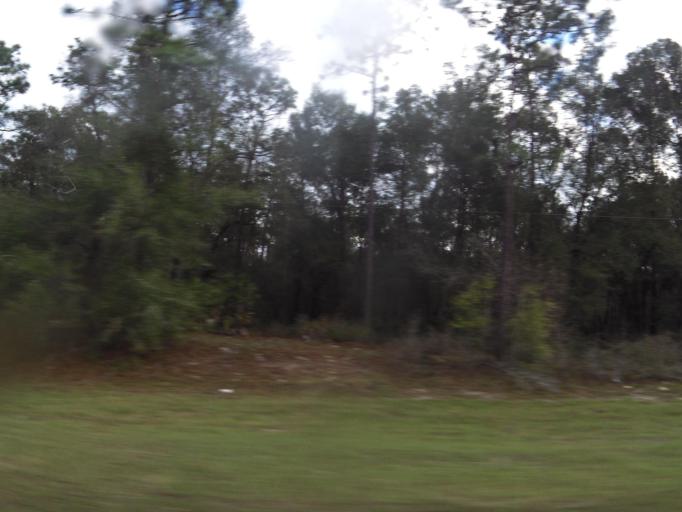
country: US
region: Florida
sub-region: Volusia County
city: Orange City
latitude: 28.9588
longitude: -81.2634
